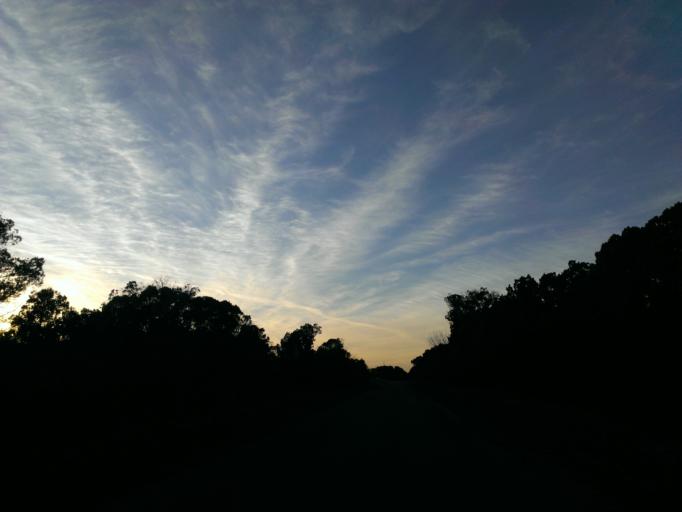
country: US
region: Texas
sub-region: Burnet County
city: Bertram
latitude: 30.7222
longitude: -98.0750
